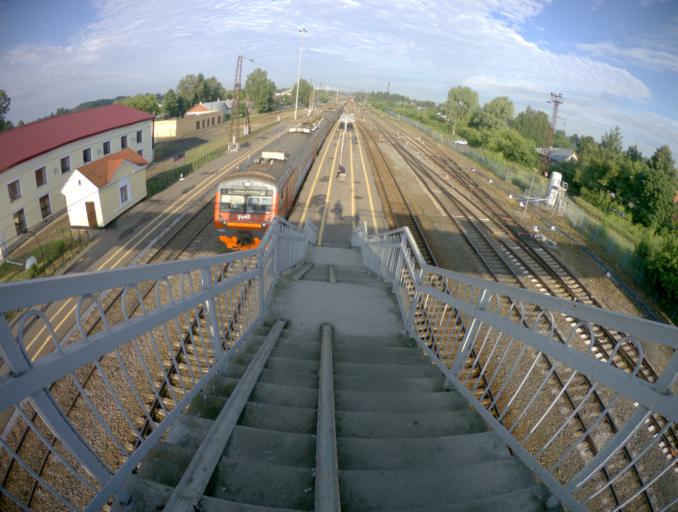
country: RU
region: Vladimir
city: Galitsy
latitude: 56.1592
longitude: 42.8137
